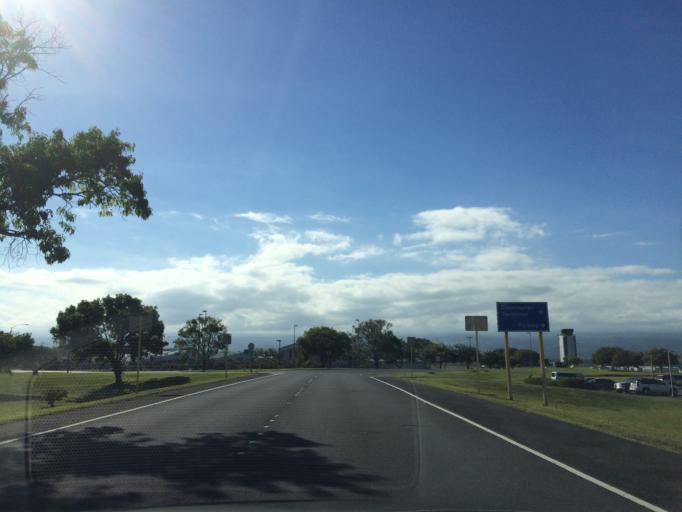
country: US
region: Hawaii
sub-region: Hawaii County
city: Hilo
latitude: 19.7145
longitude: -155.0428
